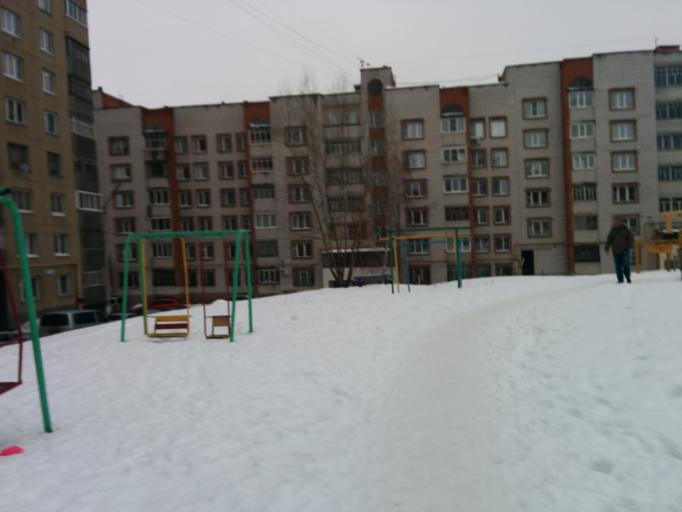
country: RU
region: Chuvashia
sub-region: Cheboksarskiy Rayon
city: Cheboksary
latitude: 56.1447
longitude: 47.2327
